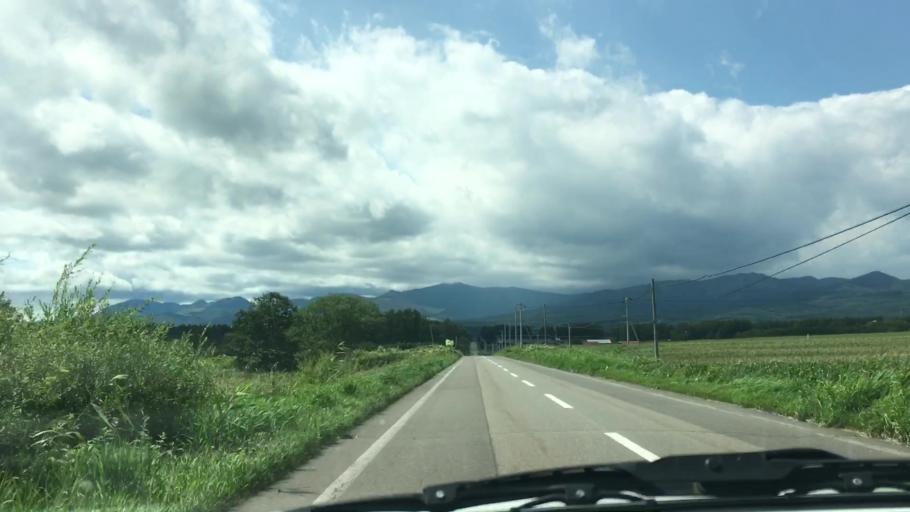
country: JP
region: Hokkaido
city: Otofuke
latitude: 43.2798
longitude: 143.3424
